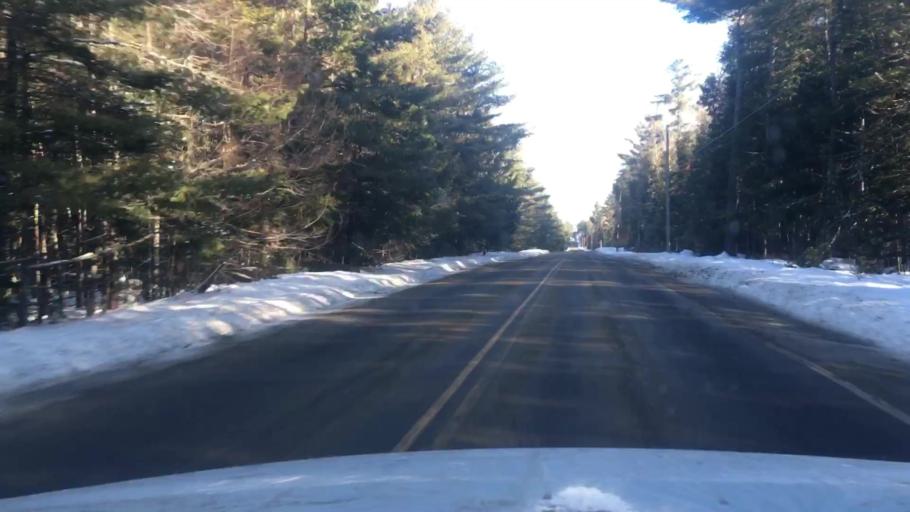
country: US
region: Maine
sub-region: Hancock County
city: Ellsworth
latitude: 44.6654
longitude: -68.3557
